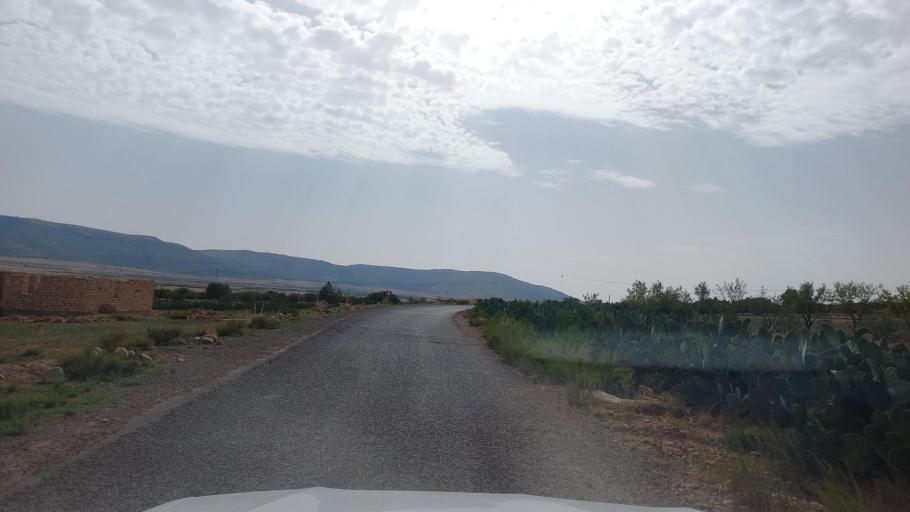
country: TN
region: Al Qasrayn
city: Kasserine
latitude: 35.3635
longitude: 8.8520
